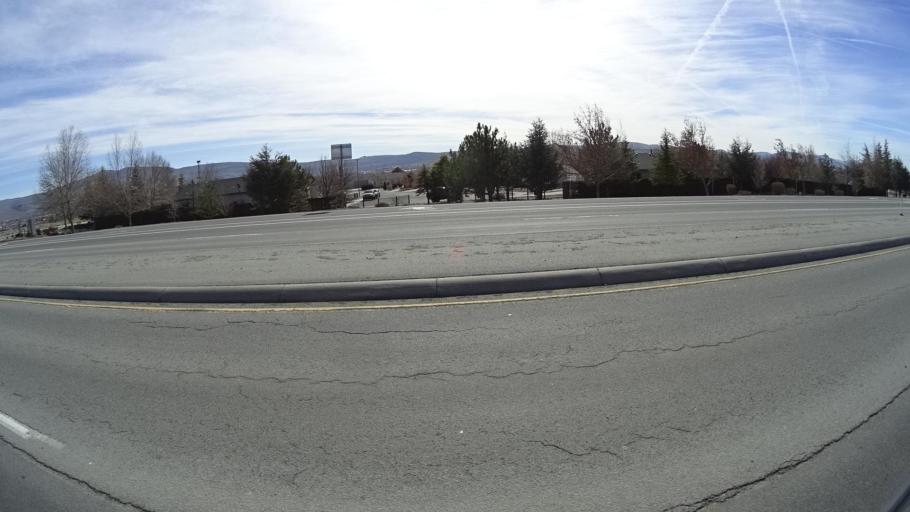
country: US
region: Nevada
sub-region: Washoe County
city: Spanish Springs
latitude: 39.6233
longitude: -119.7240
